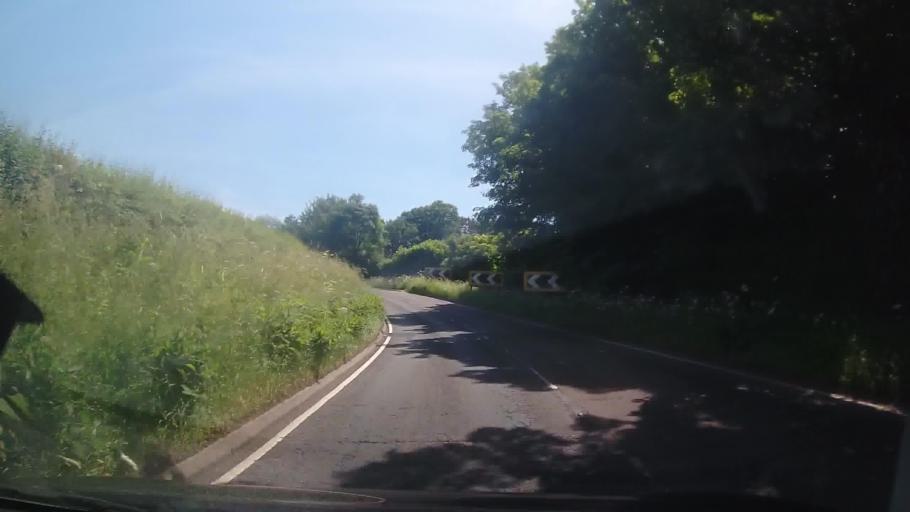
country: GB
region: England
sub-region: Bath and North East Somerset
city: Corston
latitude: 51.3838
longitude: -2.4289
